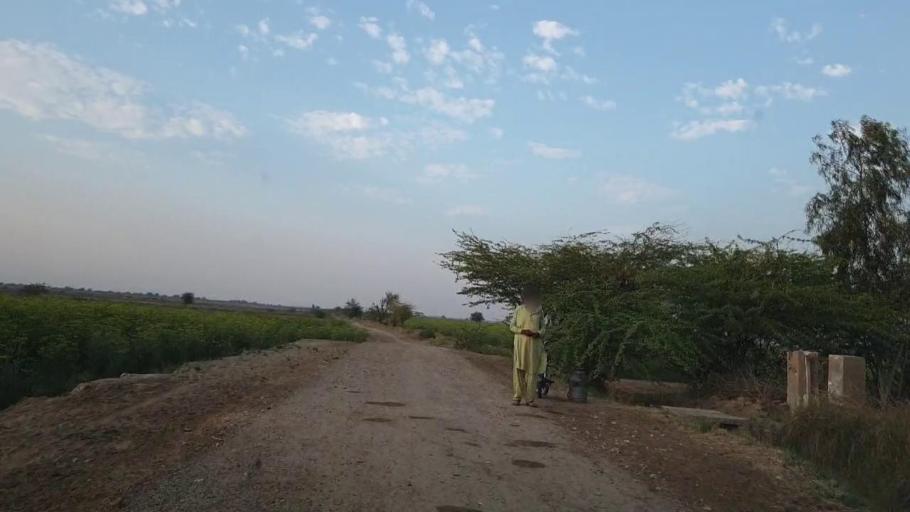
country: PK
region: Sindh
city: Pithoro
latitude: 25.6006
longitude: 69.3101
